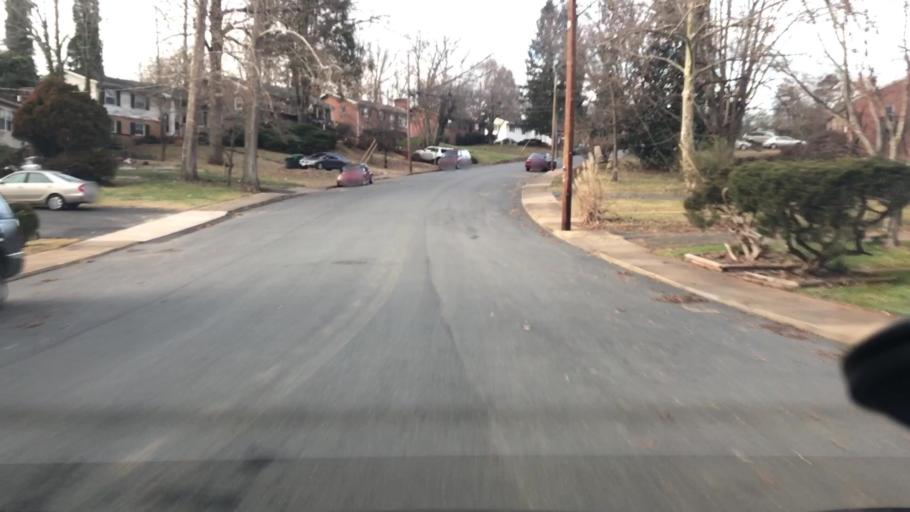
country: US
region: Virginia
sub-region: City of Charlottesville
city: Charlottesville
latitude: 38.0205
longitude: -78.5178
